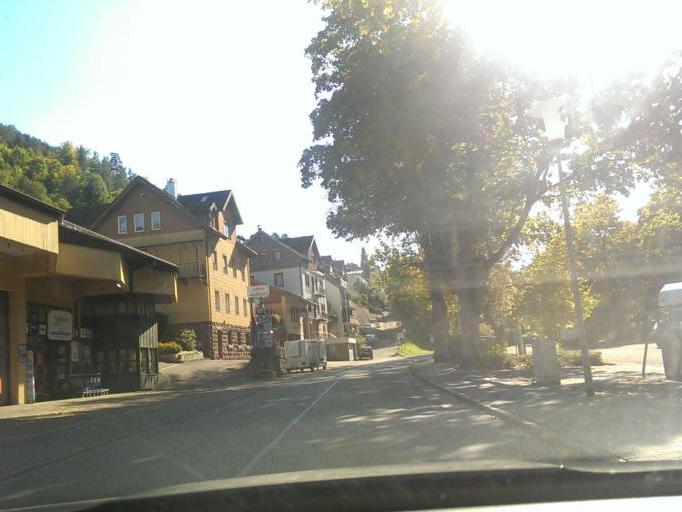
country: DE
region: Baden-Wuerttemberg
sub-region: Karlsruhe Region
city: Bad Wildbad
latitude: 48.7415
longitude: 8.5476
